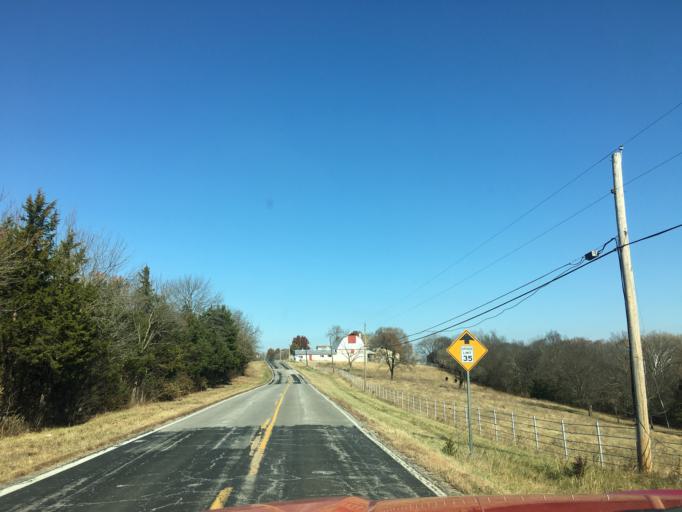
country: US
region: Missouri
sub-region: Cole County
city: Wardsville
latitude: 38.4768
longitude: -92.1774
